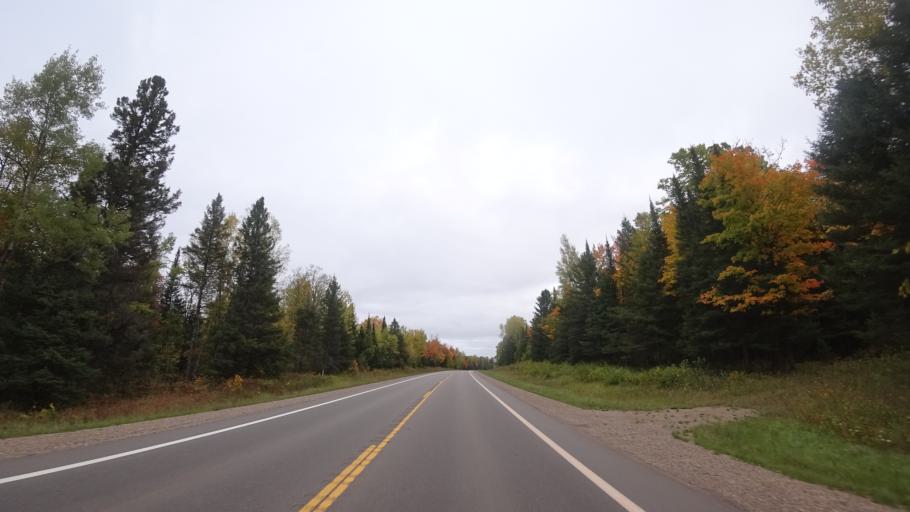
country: US
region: Michigan
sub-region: Iron County
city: Crystal Falls
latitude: 46.1646
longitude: -88.0752
